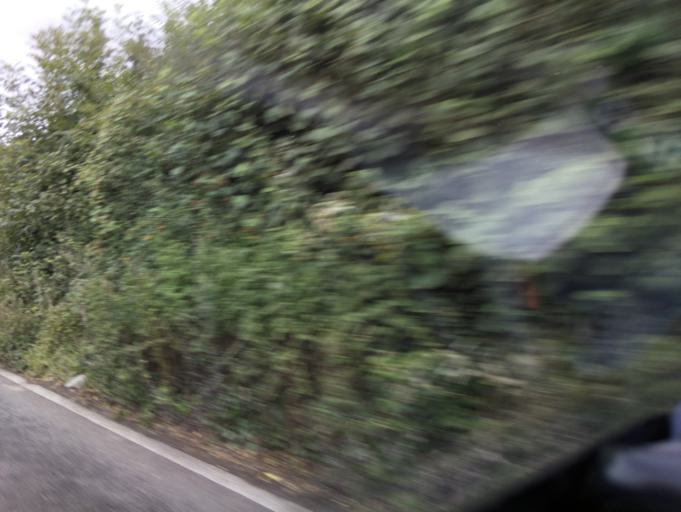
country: GB
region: England
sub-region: Devon
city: Exminster
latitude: 50.6493
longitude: -3.4817
